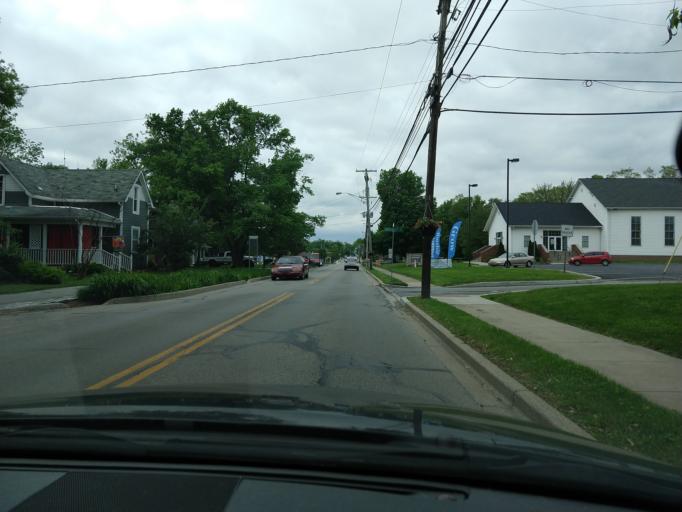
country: US
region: Indiana
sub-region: Hamilton County
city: Westfield
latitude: 40.0390
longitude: -86.1277
